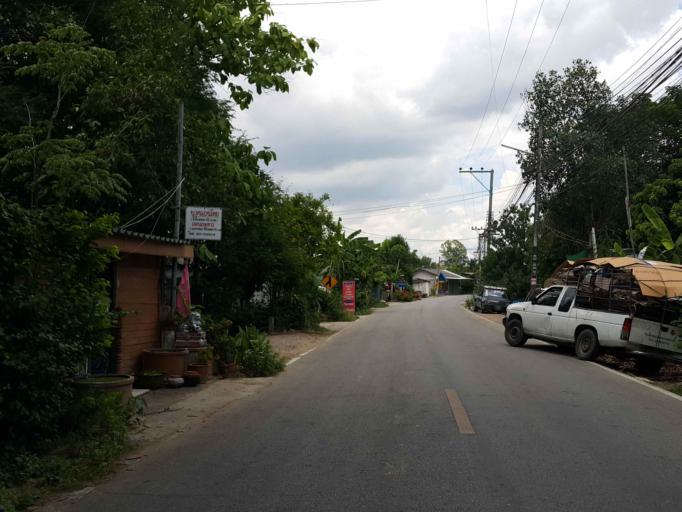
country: TH
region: Chiang Mai
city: Saraphi
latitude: 18.7378
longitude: 98.9965
